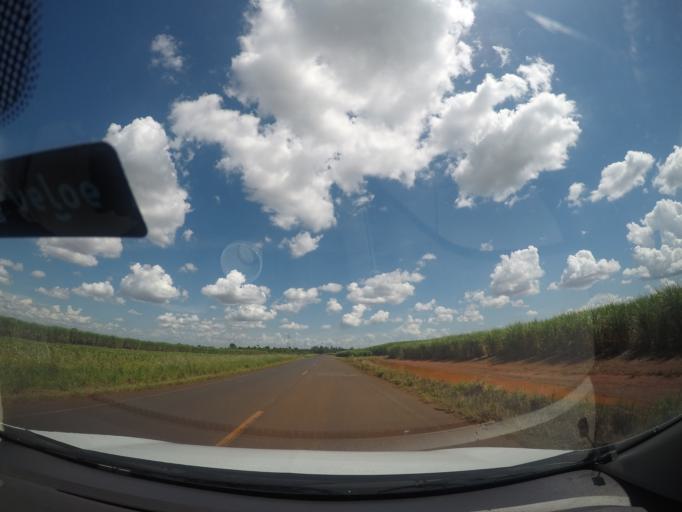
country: BR
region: Minas Gerais
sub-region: Frutal
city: Frutal
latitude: -19.8322
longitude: -48.7346
